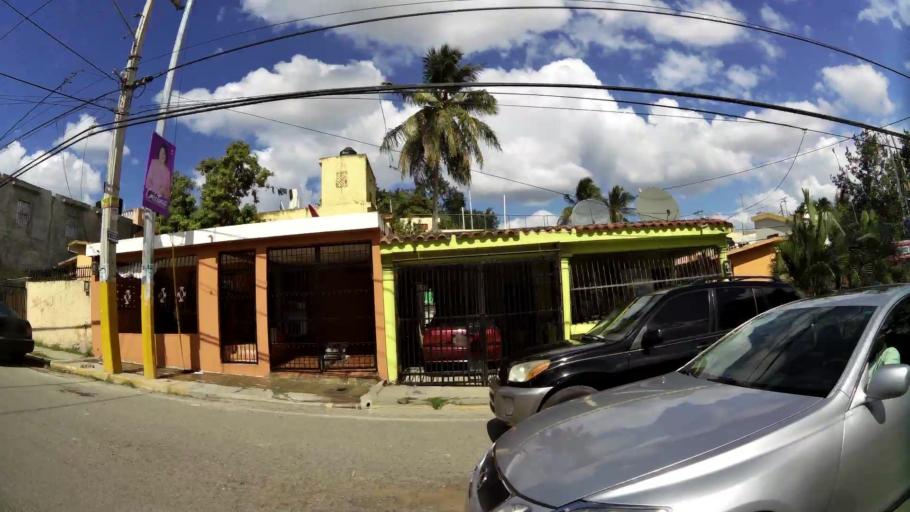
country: DO
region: Nacional
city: Ensanche Luperon
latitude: 18.5374
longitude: -69.8990
